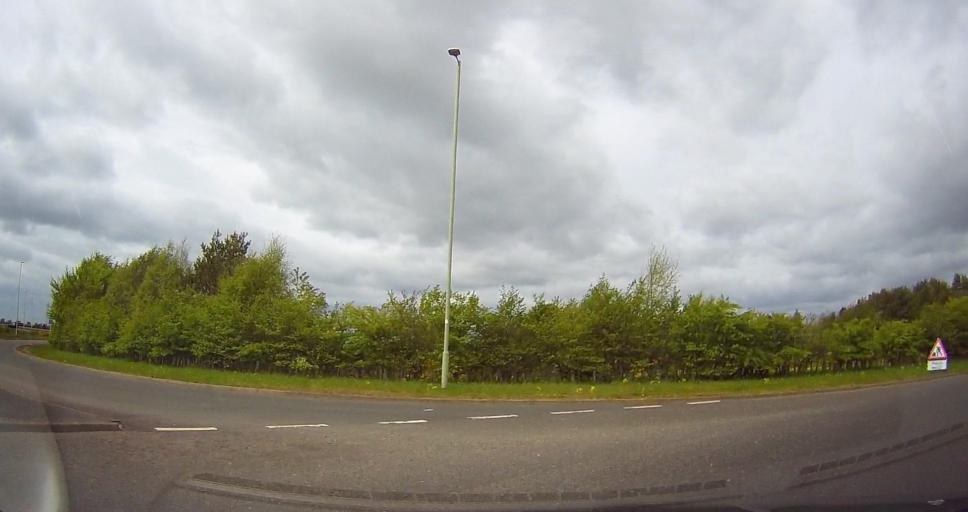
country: GB
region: Scotland
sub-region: Angus
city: Forfar
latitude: 56.6526
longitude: -2.9180
